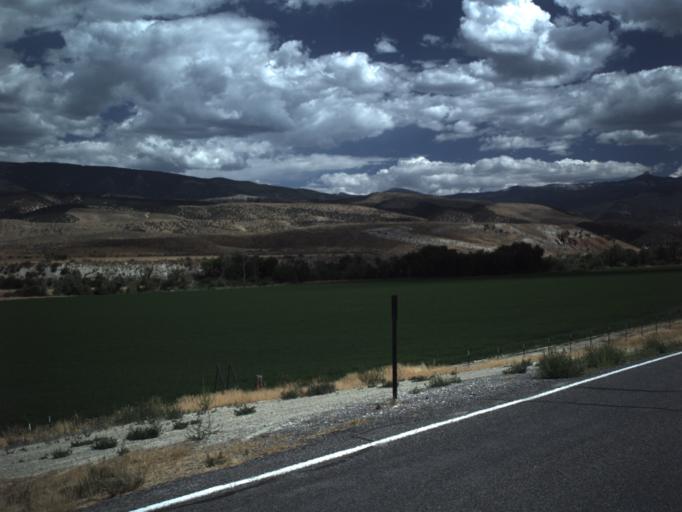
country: US
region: Utah
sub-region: Sanpete County
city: Gunnison
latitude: 39.1423
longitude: -111.7336
